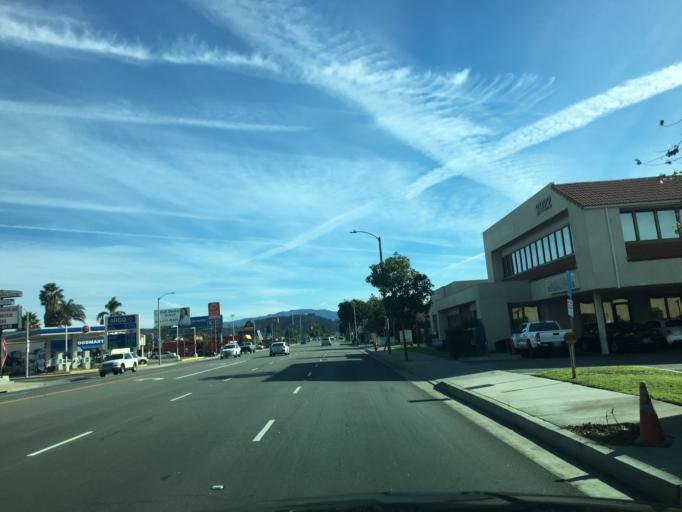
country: US
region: California
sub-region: Orange County
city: Villa Park
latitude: 33.7877
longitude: -117.8231
